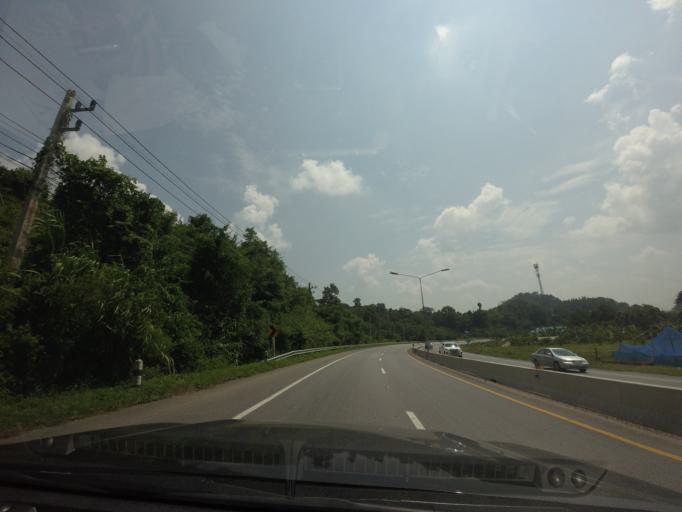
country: TH
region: Uttaradit
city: Lap Lae
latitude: 17.7761
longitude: 100.1299
